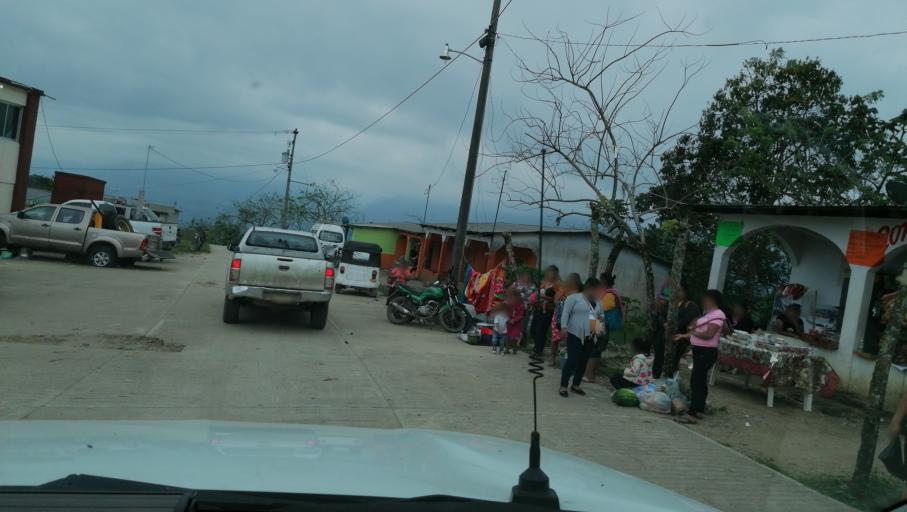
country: MX
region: Chiapas
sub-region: Francisco Leon
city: San Miguel la Sardina
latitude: 17.2857
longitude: -93.2732
